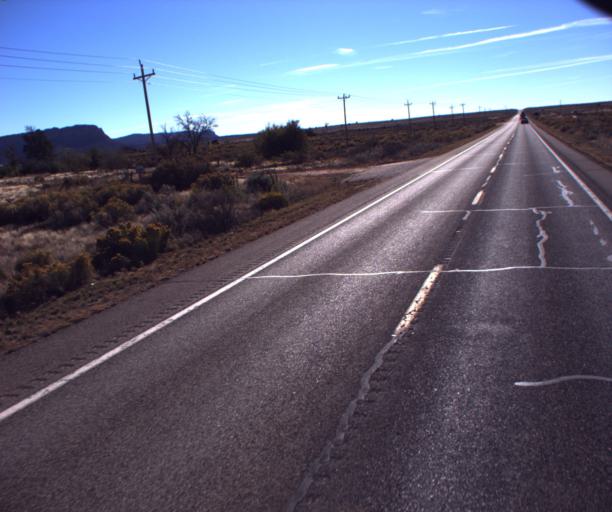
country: US
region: Arizona
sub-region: Mohave County
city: Colorado City
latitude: 36.9271
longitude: -112.9406
